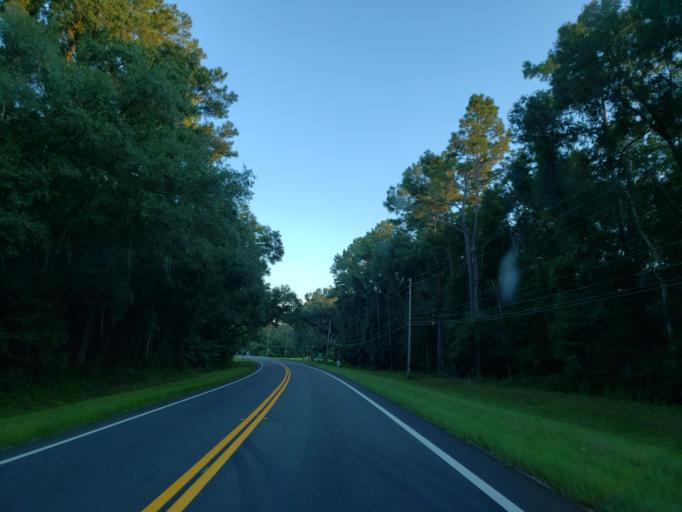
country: US
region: Florida
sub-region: Marion County
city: Citra
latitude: 29.3828
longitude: -82.2056
